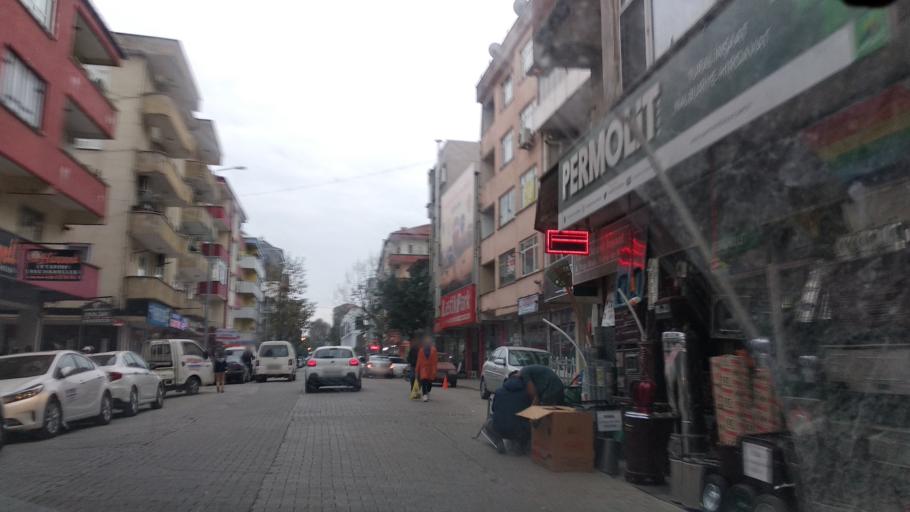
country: TR
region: Sakarya
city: Karasu
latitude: 41.0948
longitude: 30.6884
